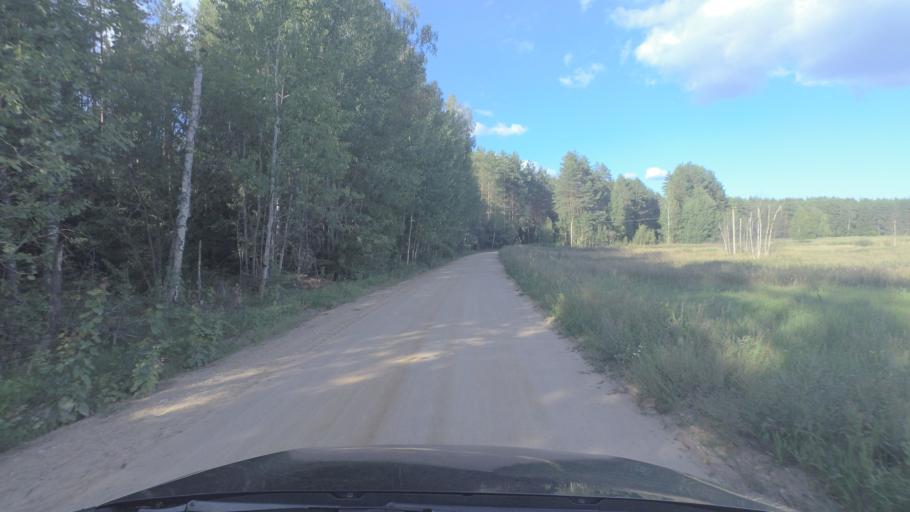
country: LT
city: Pabrade
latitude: 55.1438
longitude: 25.7389
